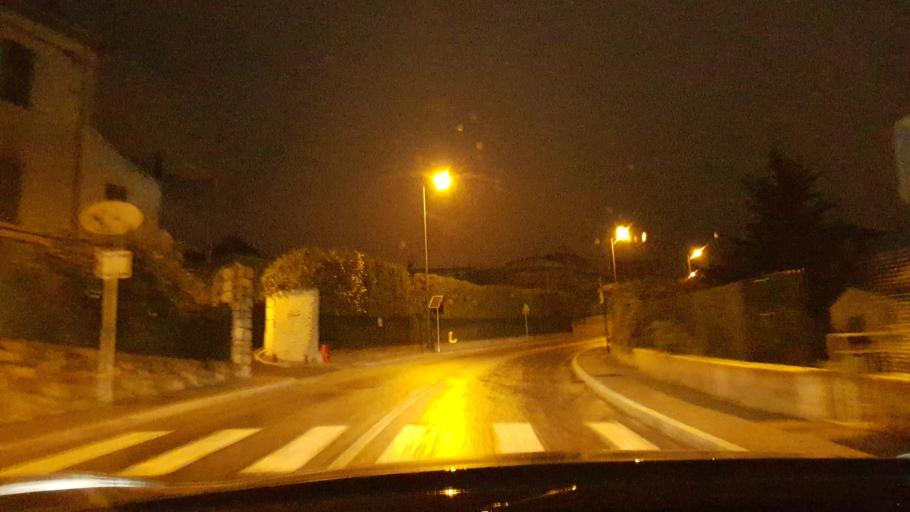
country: FR
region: Provence-Alpes-Cote d'Azur
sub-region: Departement des Alpes-Maritimes
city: Vallauris
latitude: 43.5800
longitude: 7.0499
